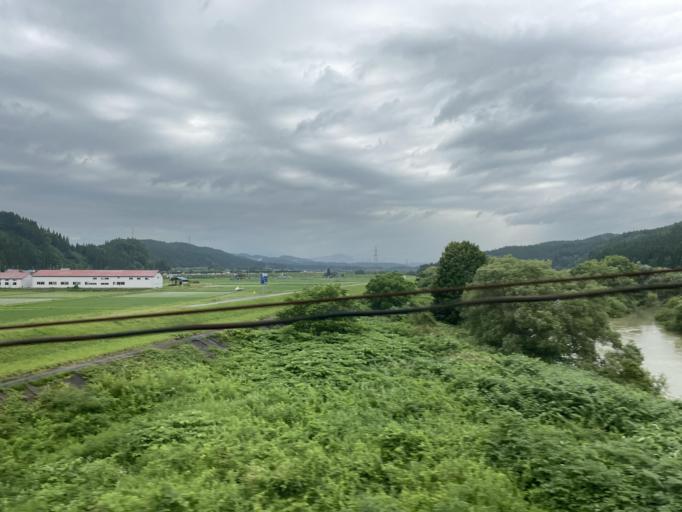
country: JP
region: Akita
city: Takanosu
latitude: 40.2196
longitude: 140.2490
